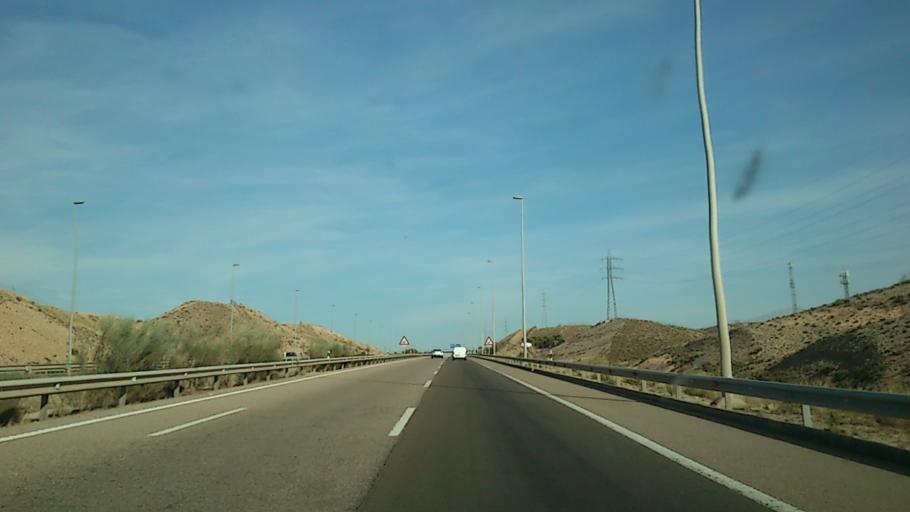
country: ES
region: Aragon
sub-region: Provincia de Zaragoza
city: Cuarte de Huerva
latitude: 41.6078
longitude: -0.9119
